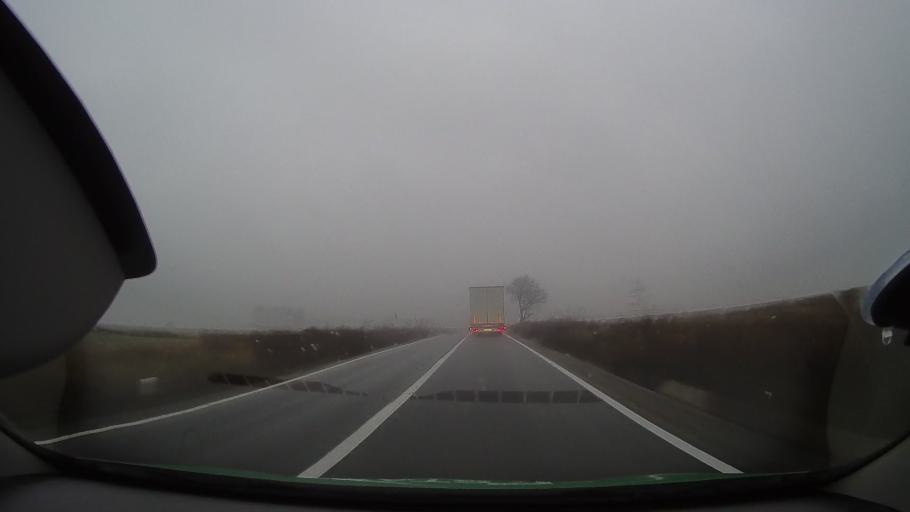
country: RO
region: Bihor
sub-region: Comuna Olcea
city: Olcea
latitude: 46.6702
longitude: 21.9643
